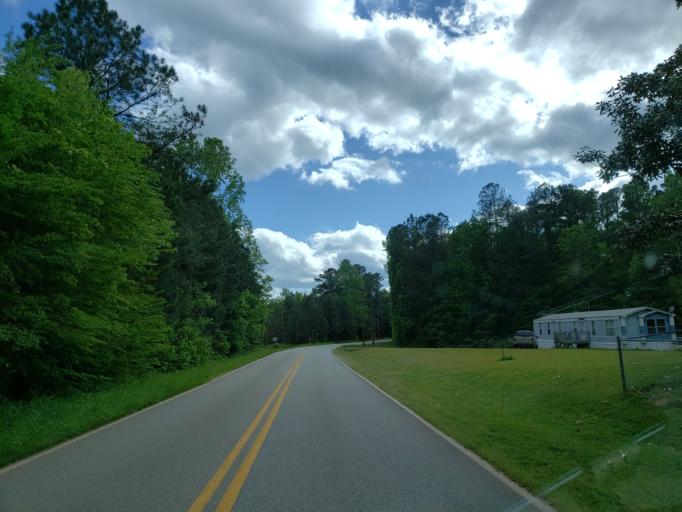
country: US
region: Georgia
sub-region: Carroll County
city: Mount Zion
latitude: 33.6669
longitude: -85.1976
